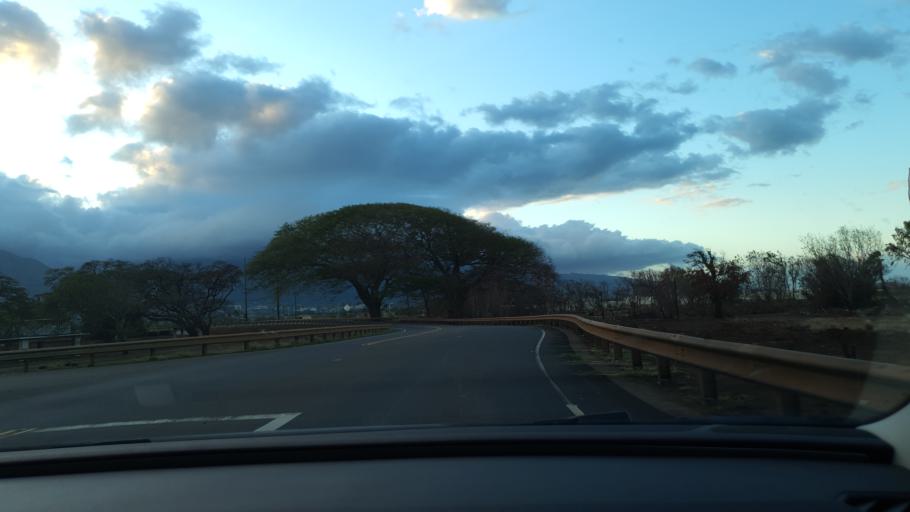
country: US
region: Hawaii
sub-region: Maui County
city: Kahului
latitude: 20.8693
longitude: -156.4520
